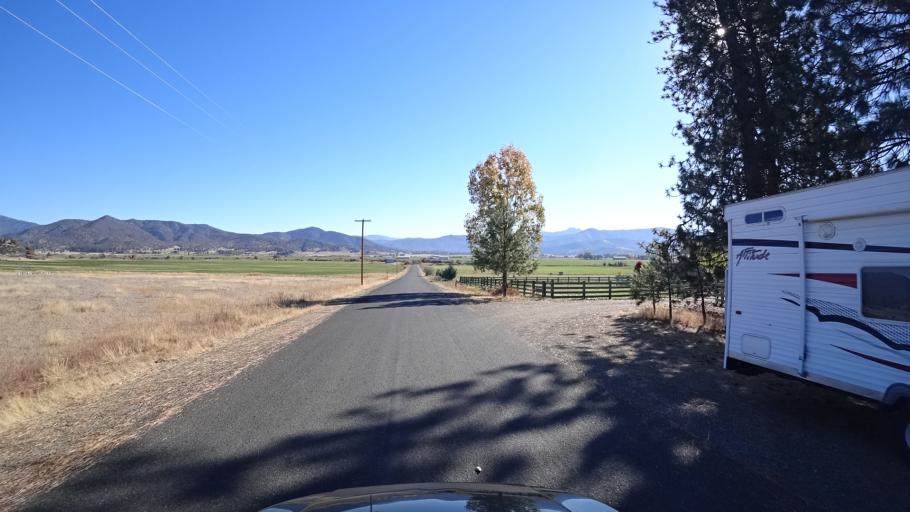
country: US
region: California
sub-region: Siskiyou County
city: Yreka
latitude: 41.5777
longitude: -122.8676
